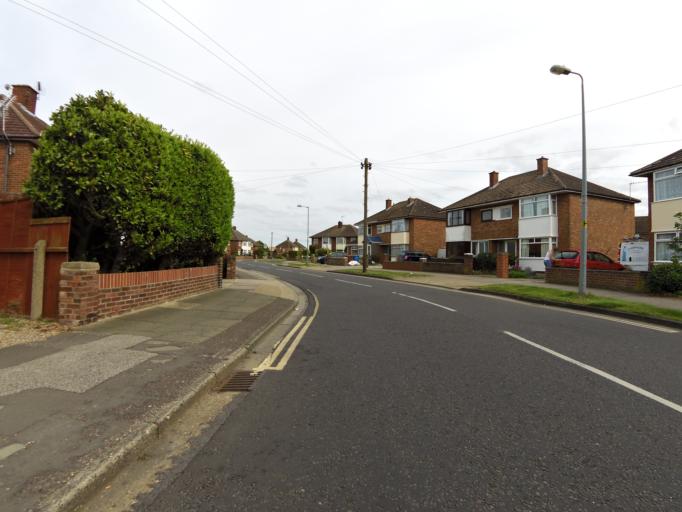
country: GB
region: England
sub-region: Suffolk
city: Ipswich
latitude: 52.0324
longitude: 1.1847
